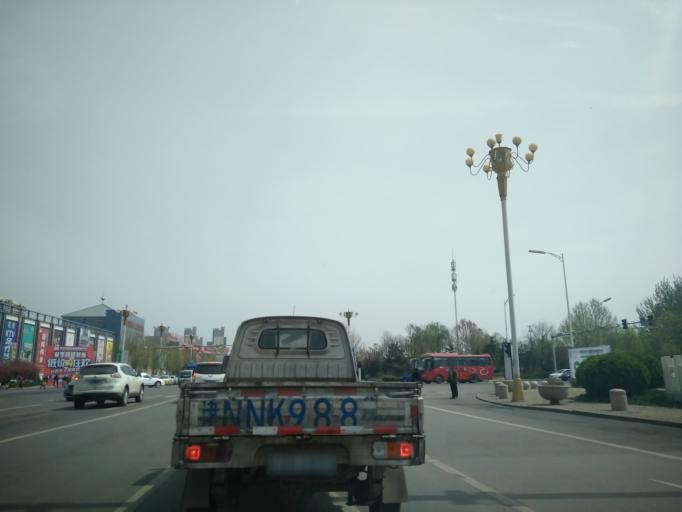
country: CN
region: Beijing
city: Xiji
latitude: 39.7461
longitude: 116.9864
